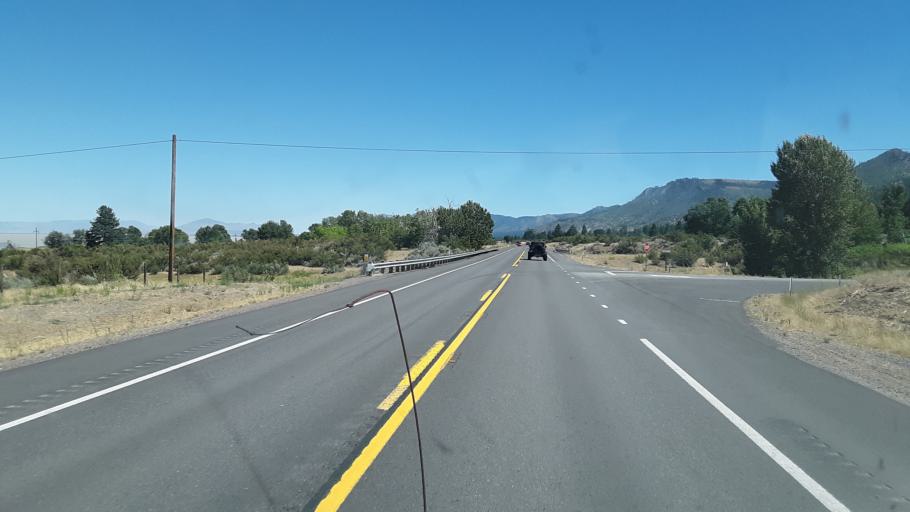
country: US
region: California
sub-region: Lassen County
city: Janesville
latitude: 40.2765
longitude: -120.4841
